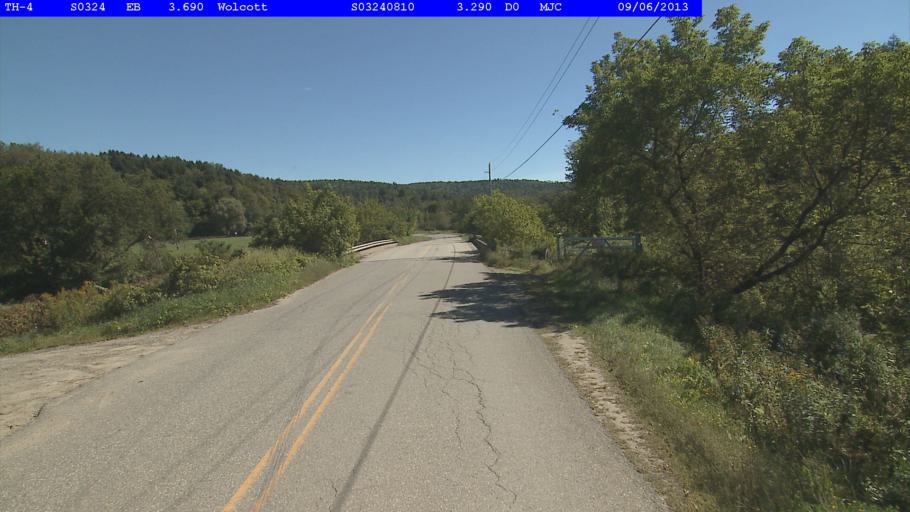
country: US
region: Vermont
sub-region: Lamoille County
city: Morrisville
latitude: 44.5514
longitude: -72.4788
